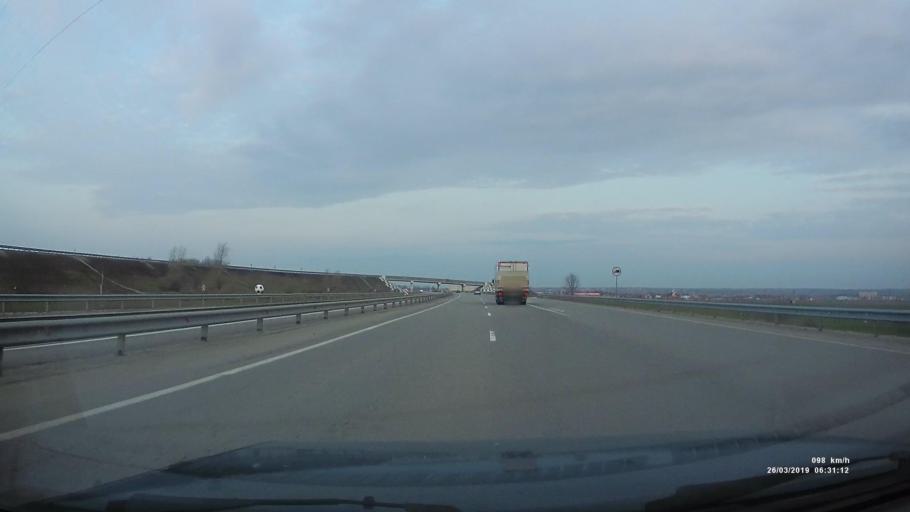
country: RU
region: Rostov
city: Krym
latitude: 47.2731
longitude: 39.5367
